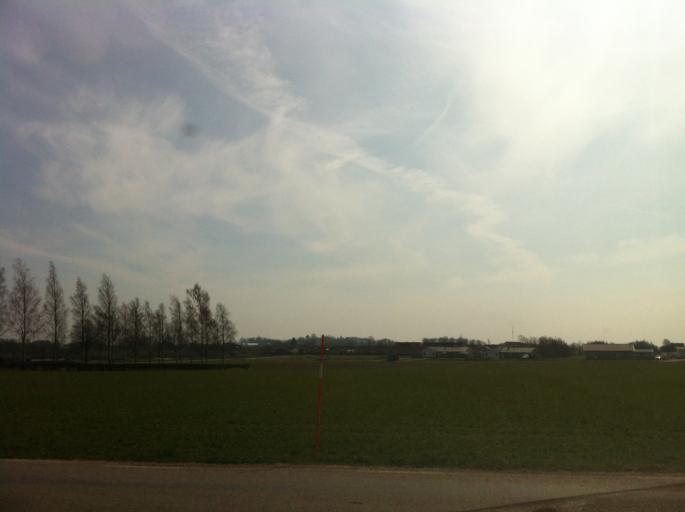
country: SE
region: Skane
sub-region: Svalovs Kommun
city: Svaloev
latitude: 55.9251
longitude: 13.1020
